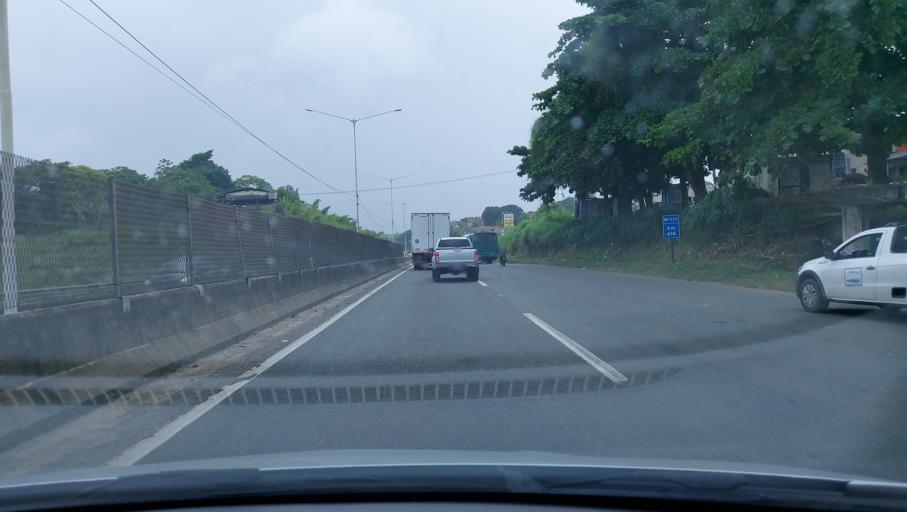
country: BR
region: Bahia
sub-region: Simoes Filho
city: Simoes Filho
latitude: -12.8869
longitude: -38.4392
